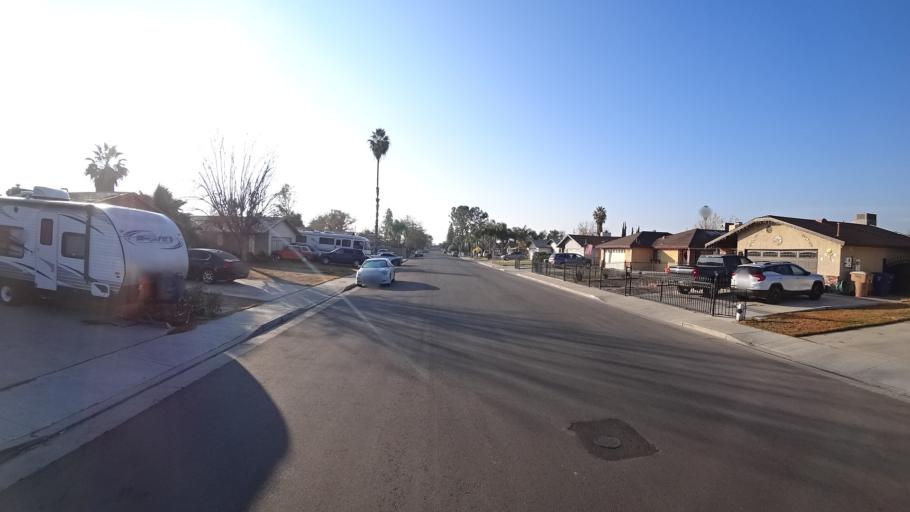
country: US
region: California
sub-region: Kern County
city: Greenfield
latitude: 35.3056
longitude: -119.0229
